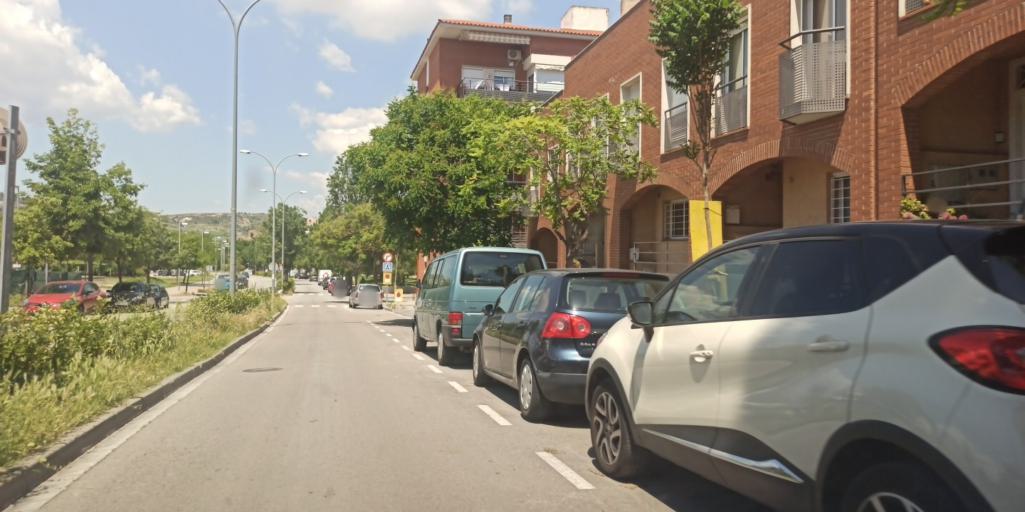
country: ES
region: Catalonia
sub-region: Provincia de Barcelona
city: Vilafranca del Penedes
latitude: 41.3451
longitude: 1.6909
